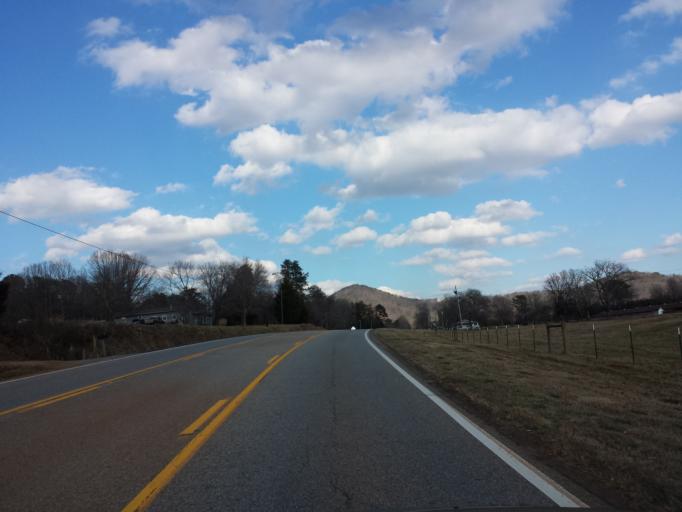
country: US
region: Georgia
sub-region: White County
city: Cleveland
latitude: 34.5474
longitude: -83.8025
